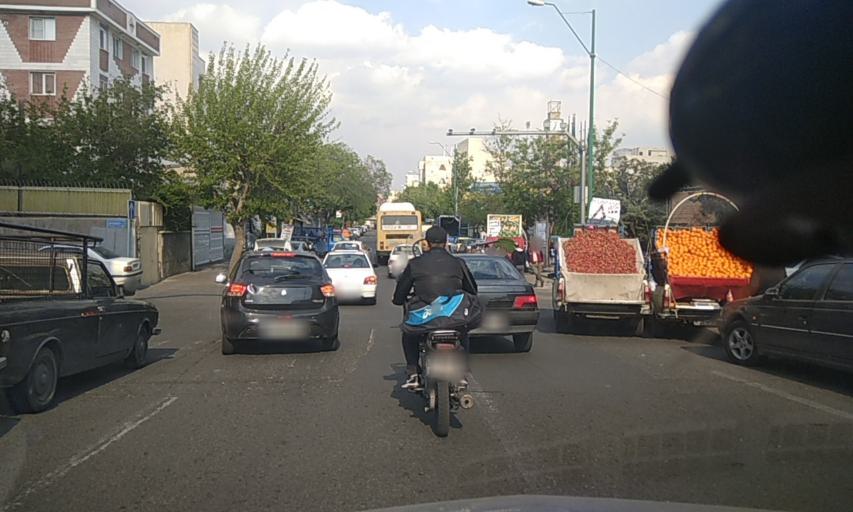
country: IR
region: Tehran
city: Tehran
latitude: 35.6819
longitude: 51.3804
